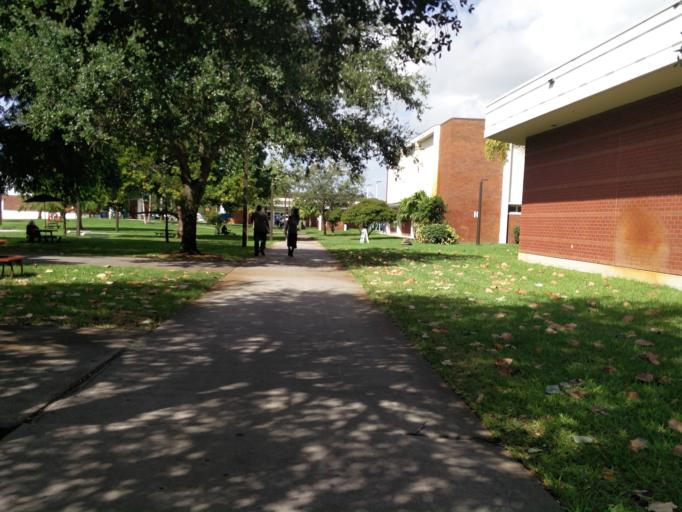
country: US
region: Florida
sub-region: Broward County
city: Davie
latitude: 26.0814
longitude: -80.2354
